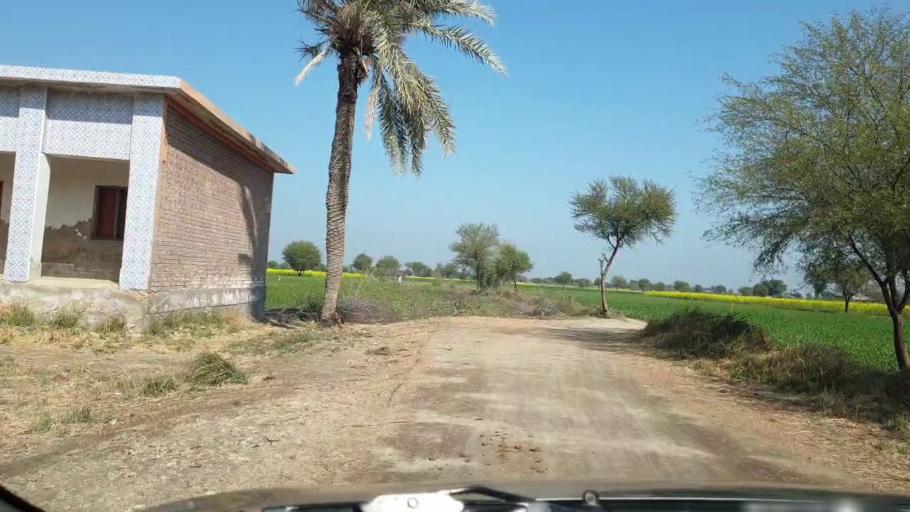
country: PK
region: Sindh
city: Sinjhoro
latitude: 25.9541
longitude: 68.7643
